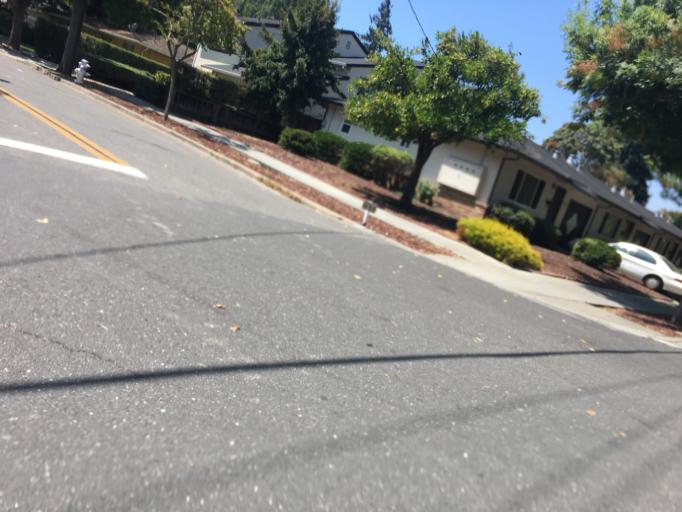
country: US
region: California
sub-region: Santa Clara County
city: Mountain View
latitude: 37.3964
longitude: -122.0855
